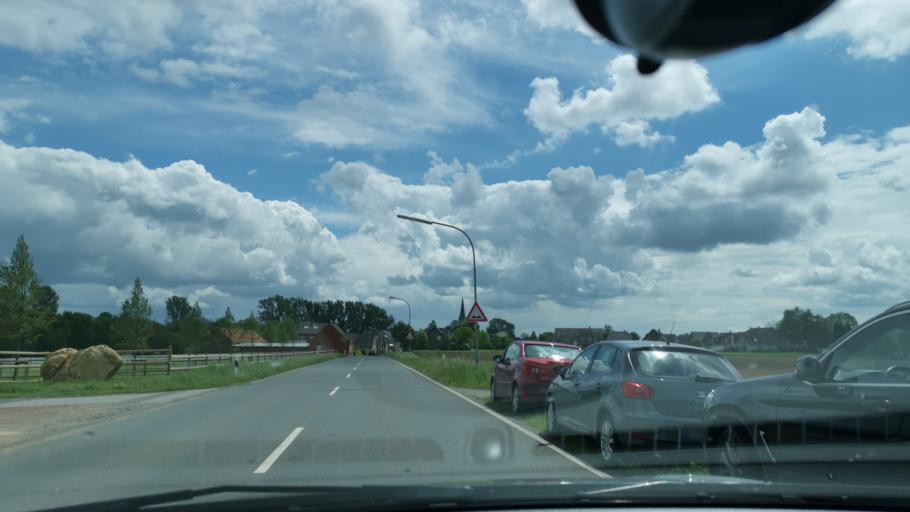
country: DE
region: North Rhine-Westphalia
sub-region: Regierungsbezirk Dusseldorf
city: Rommerskirchen
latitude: 51.0767
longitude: 6.6891
